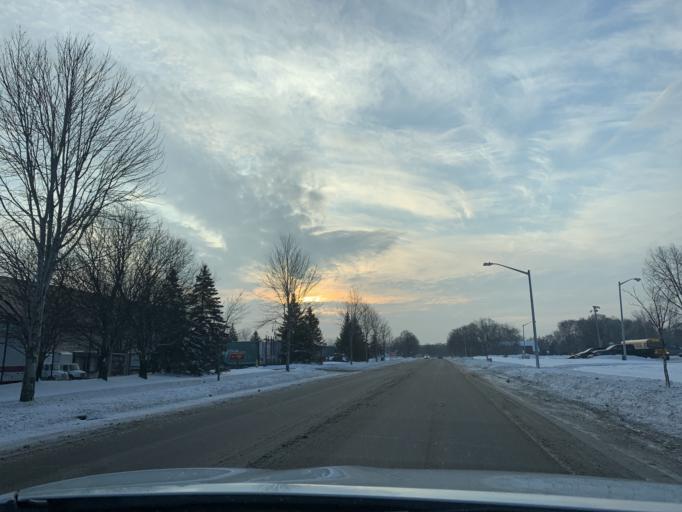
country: US
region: Minnesota
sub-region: Anoka County
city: Coon Rapids
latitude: 45.1564
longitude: -93.2821
